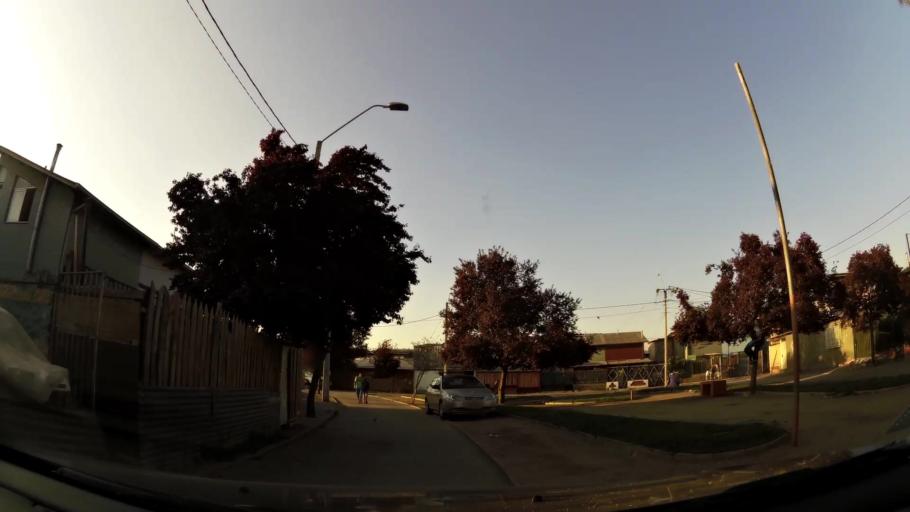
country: CL
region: Santiago Metropolitan
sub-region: Provincia de Maipo
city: San Bernardo
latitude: -33.5936
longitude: -70.6688
